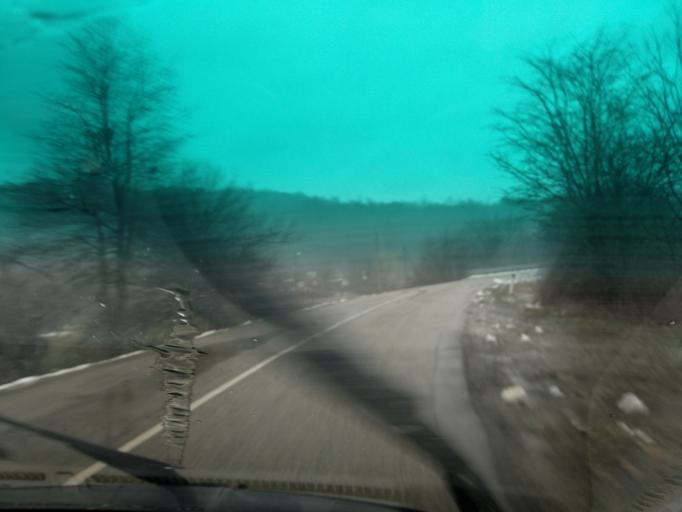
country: RU
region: Krasnodarskiy
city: Khadyzhensk
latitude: 44.2339
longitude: 39.3785
